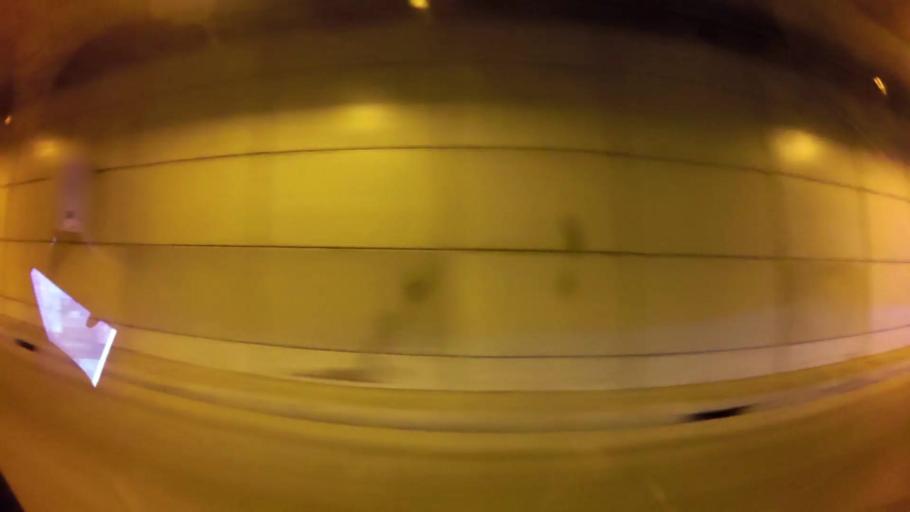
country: EC
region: Guayas
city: Eloy Alfaro
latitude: -2.1829
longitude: -79.8767
